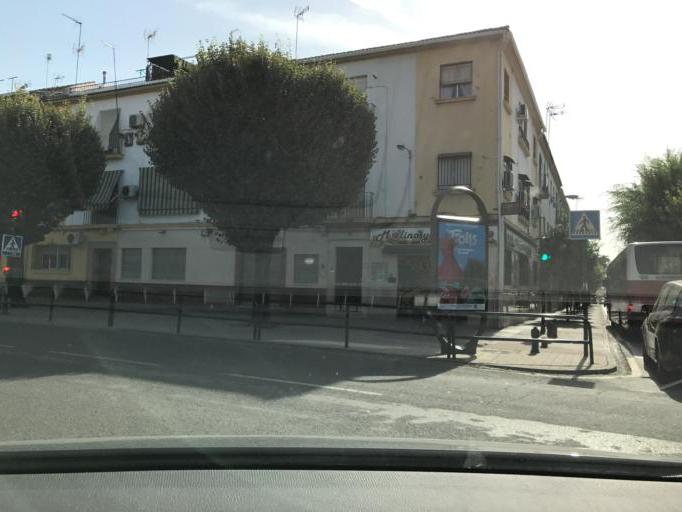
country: ES
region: Andalusia
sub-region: Provincia de Granada
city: Granada
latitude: 37.1931
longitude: -3.6236
